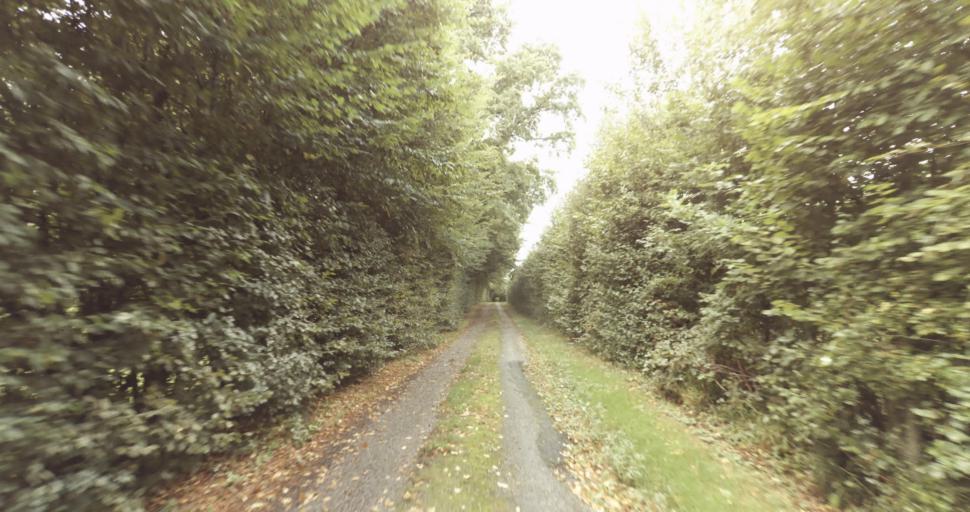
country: FR
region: Lower Normandy
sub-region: Departement de l'Orne
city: Sainte-Gauburge-Sainte-Colombe
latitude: 48.7113
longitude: 0.3882
